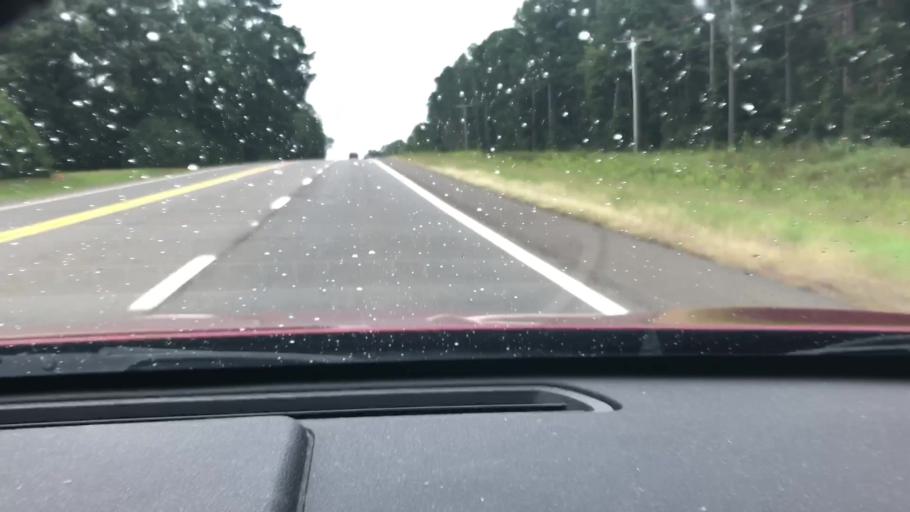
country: US
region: Arkansas
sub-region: Columbia County
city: Waldo
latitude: 33.3511
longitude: -93.3788
